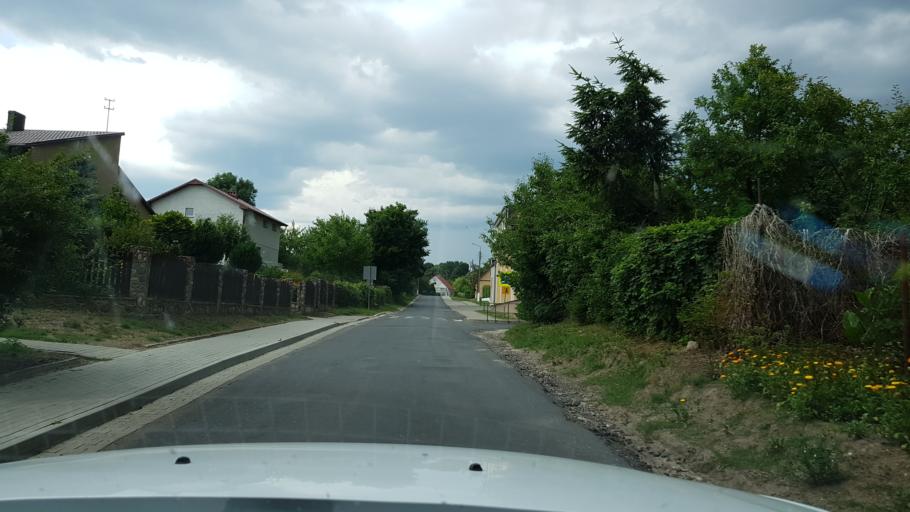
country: PL
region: West Pomeranian Voivodeship
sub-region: Powiat walecki
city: Walcz
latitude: 53.1973
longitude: 16.4944
